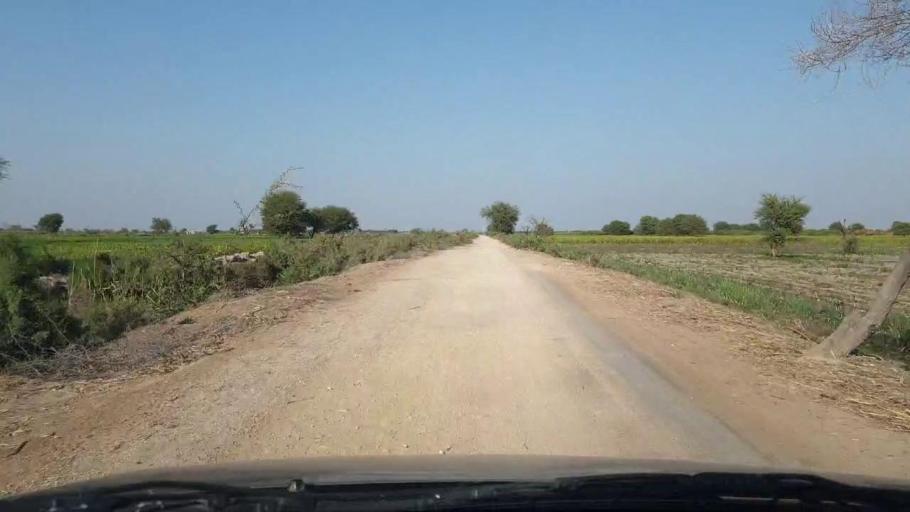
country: PK
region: Sindh
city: Digri
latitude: 25.1323
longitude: 69.2770
